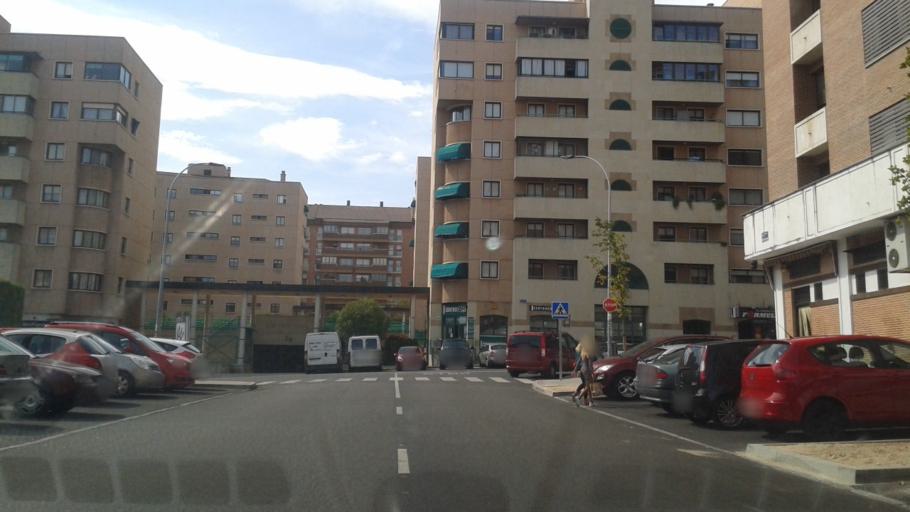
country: ES
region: Castille and Leon
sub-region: Provincia de Valladolid
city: Zaratan
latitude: 41.6352
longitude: -4.7567
